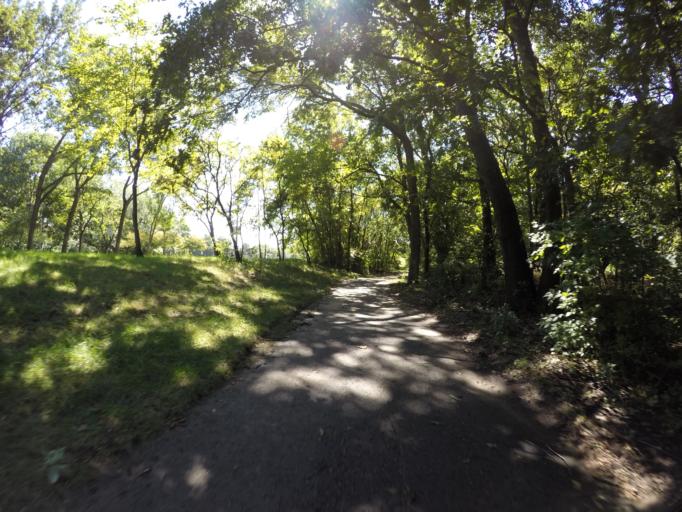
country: US
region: Kansas
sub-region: Johnson County
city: Lenexa
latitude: 38.9286
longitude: -94.6965
